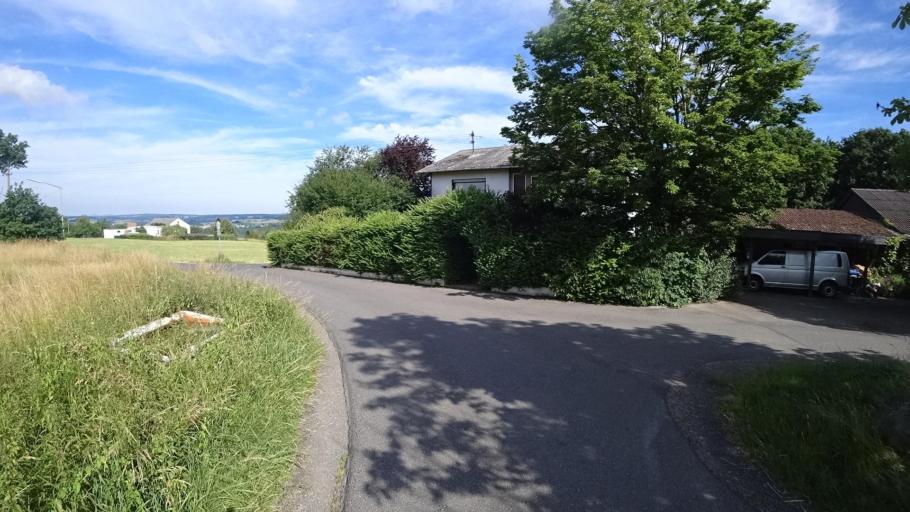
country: DE
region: Rheinland-Pfalz
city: Fluterschen
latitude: 50.6665
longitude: 7.6331
